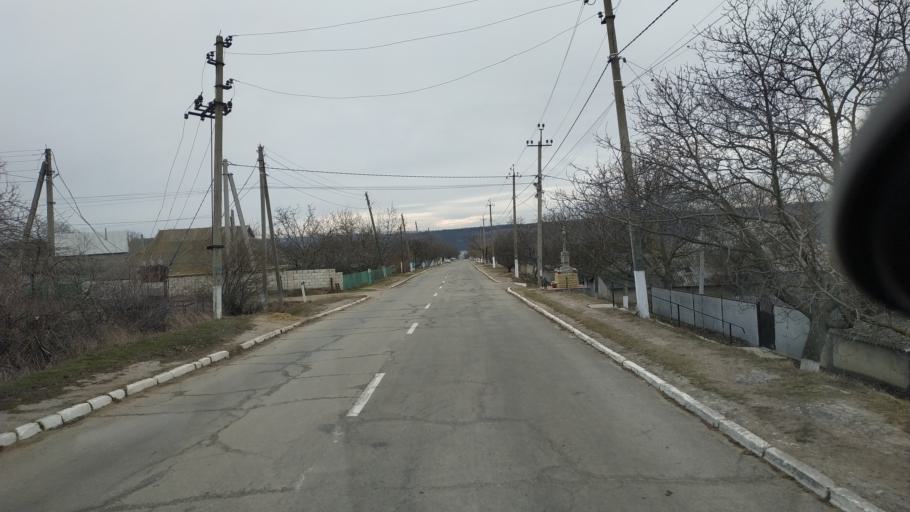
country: MD
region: Telenesti
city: Cocieri
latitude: 47.3518
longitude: 29.1170
